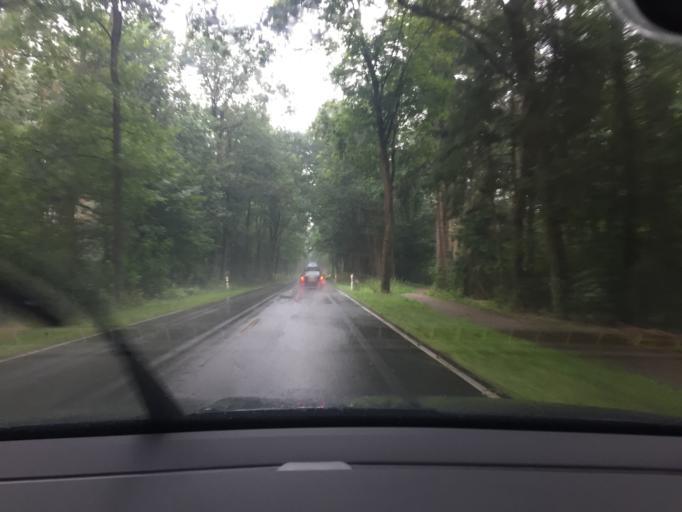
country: DE
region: Lower Saxony
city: Eickeloh
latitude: 52.7426
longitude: 9.5993
